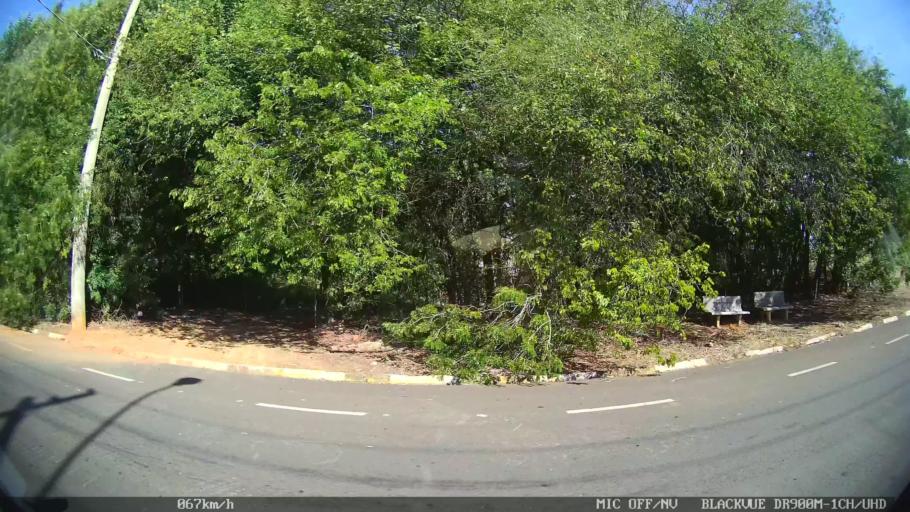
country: BR
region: Sao Paulo
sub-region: Franca
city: Franca
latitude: -20.5490
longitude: -47.4519
